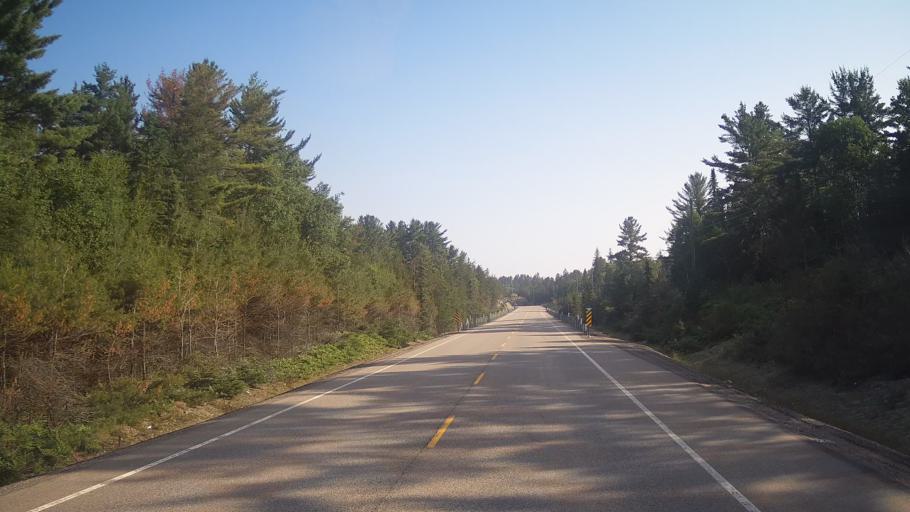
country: CA
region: Ontario
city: Rayside-Balfour
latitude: 46.7532
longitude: -81.5992
